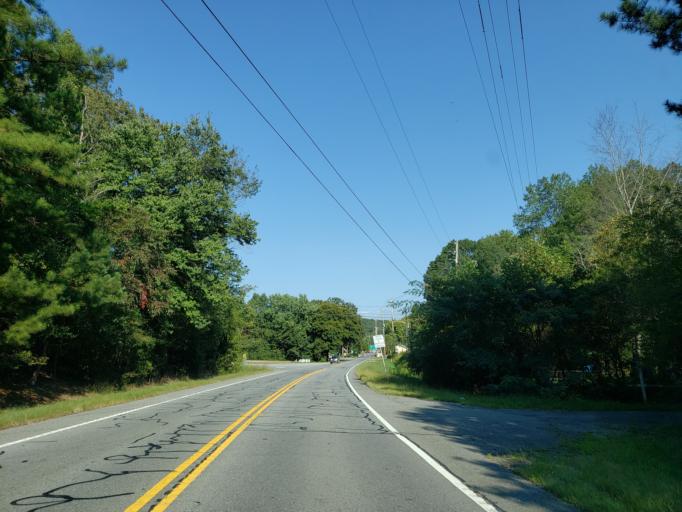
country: US
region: Georgia
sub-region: Whitfield County
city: Varnell
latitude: 34.9011
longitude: -84.9787
